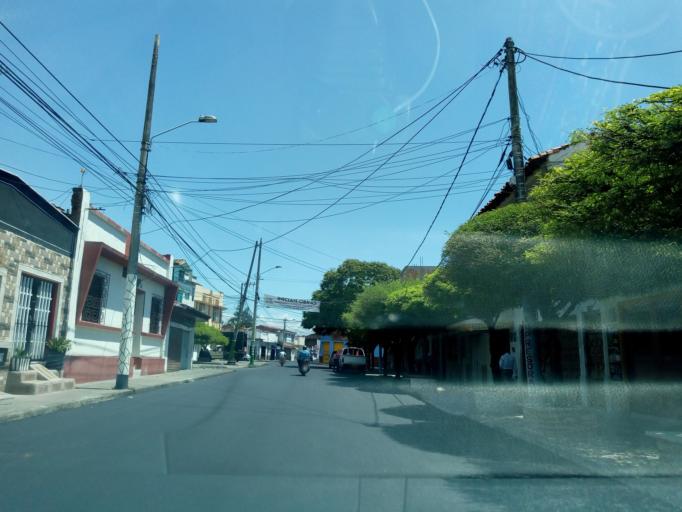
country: CO
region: Valle del Cauca
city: Cartago
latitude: 4.7447
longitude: -75.9123
